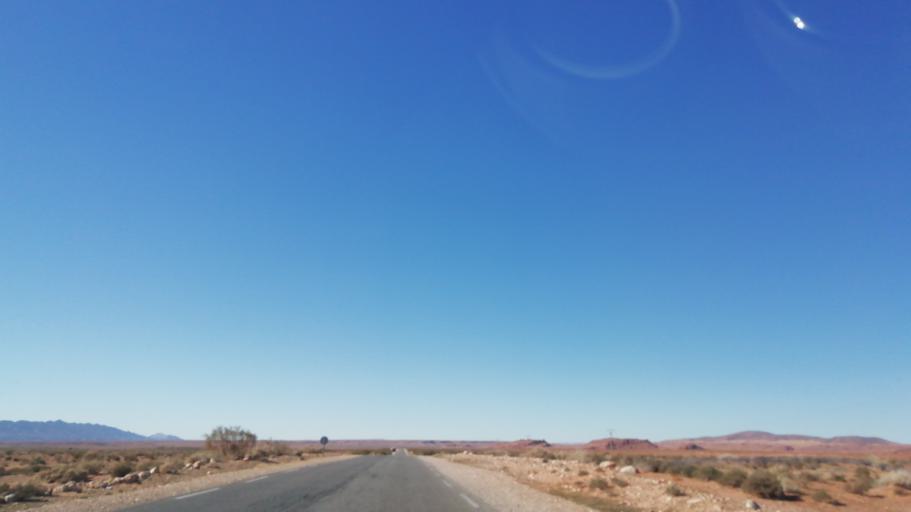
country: DZ
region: El Bayadh
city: El Abiodh Sidi Cheikh
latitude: 33.1825
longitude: 0.5527
